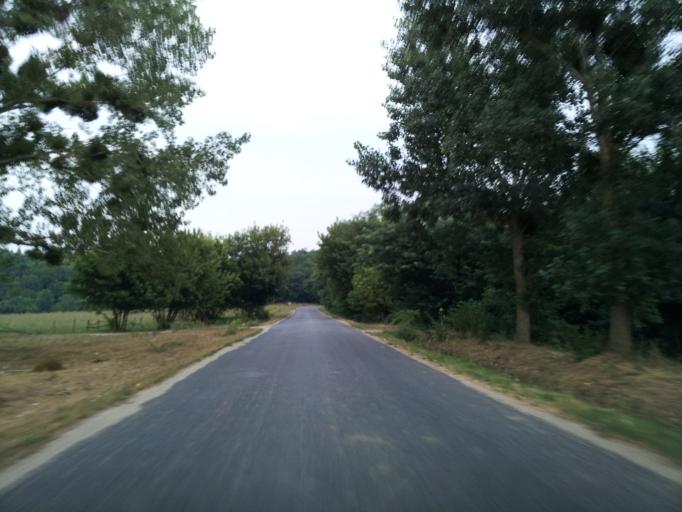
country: HU
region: Vas
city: Sarvar
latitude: 47.2063
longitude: 16.9417
